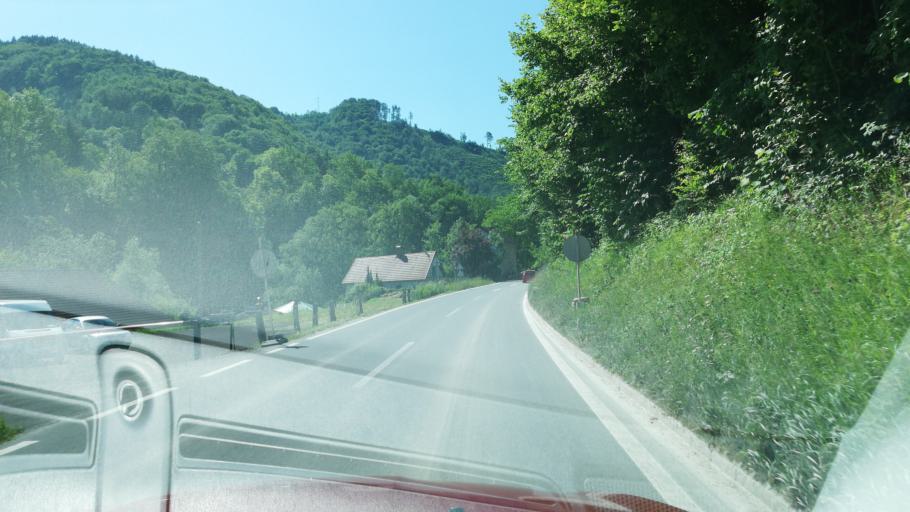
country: AT
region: Upper Austria
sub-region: Politischer Bezirk Kirchdorf an der Krems
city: Gruenburg
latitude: 47.9538
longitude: 14.2552
